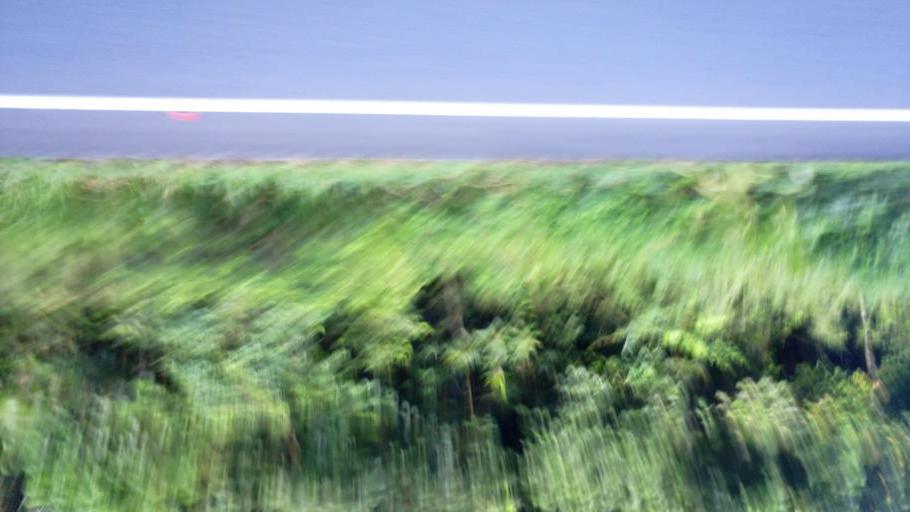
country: AU
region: Queensland
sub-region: Cassowary Coast
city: Innisfail
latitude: -17.6079
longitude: 145.7824
